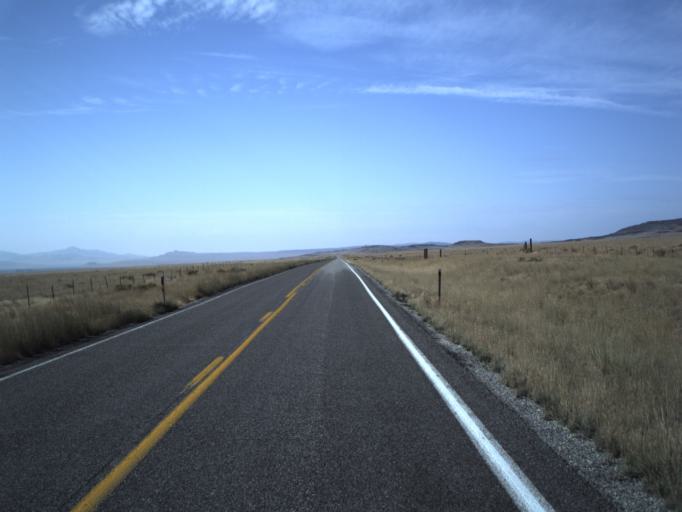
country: US
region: Idaho
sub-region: Oneida County
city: Malad City
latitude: 41.8841
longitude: -113.1157
